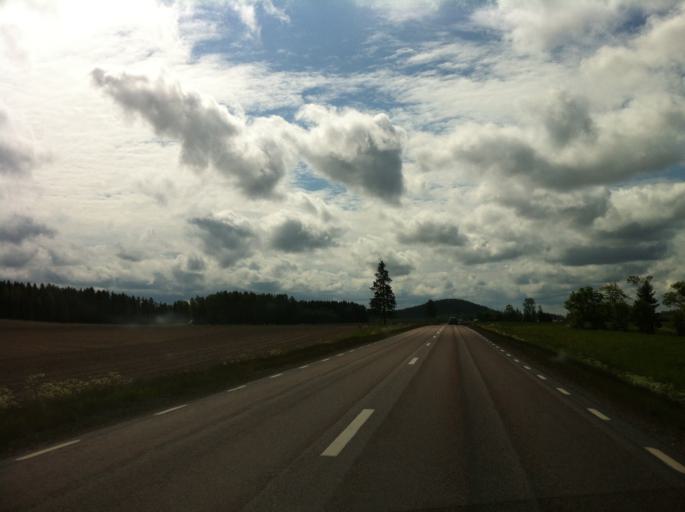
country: SE
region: Vaermland
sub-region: Sunne Kommun
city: Sunne
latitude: 59.6507
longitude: 13.1539
